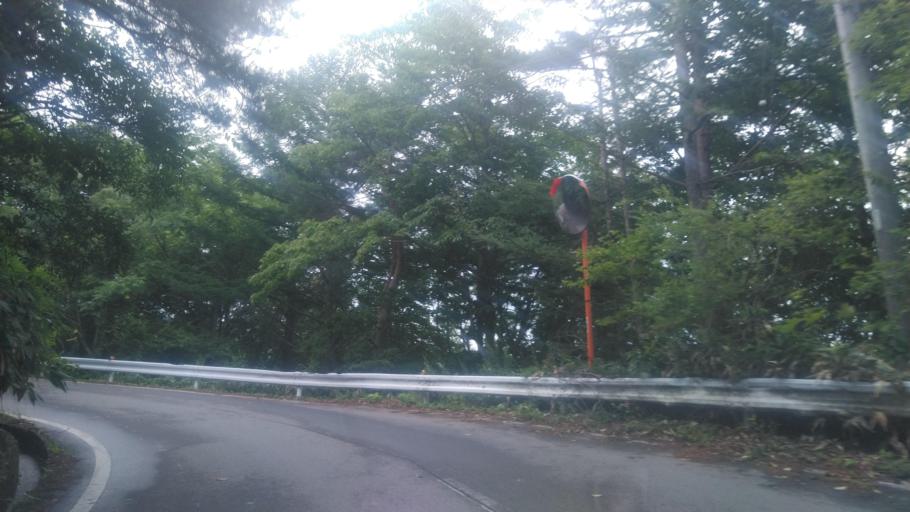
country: JP
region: Nagano
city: Ueda
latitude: 36.4970
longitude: 138.3820
